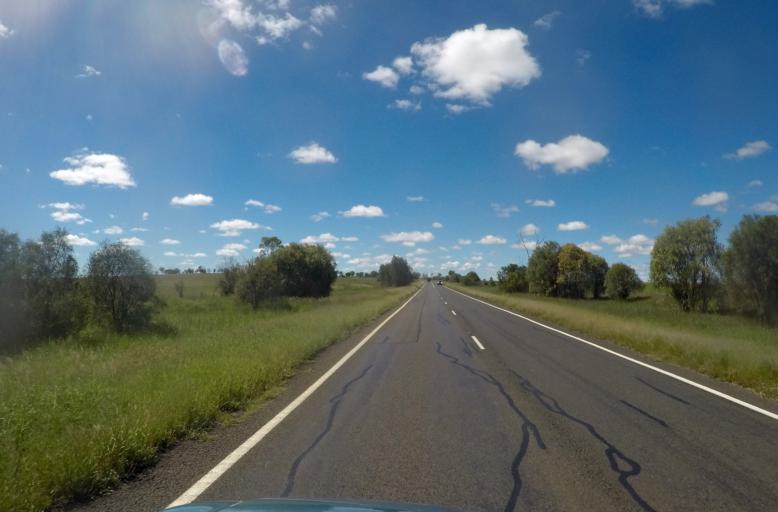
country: AU
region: Queensland
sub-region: Western Downs
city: Westcourt
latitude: -26.6453
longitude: 149.7929
